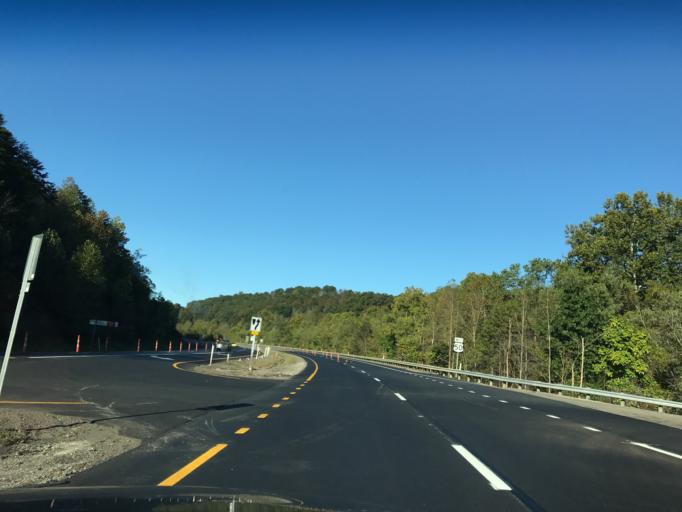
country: US
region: Ohio
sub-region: Washington County
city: Reno
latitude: 39.2476
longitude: -81.3826
